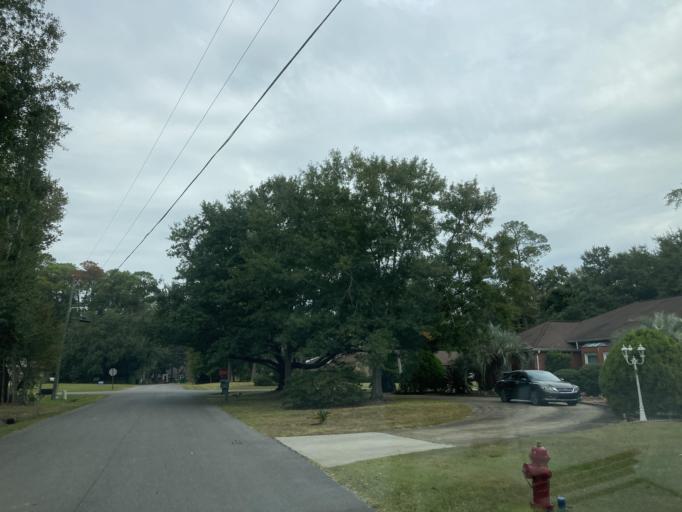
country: US
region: Mississippi
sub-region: Jackson County
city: Gulf Hills
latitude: 30.4323
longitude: -88.8418
